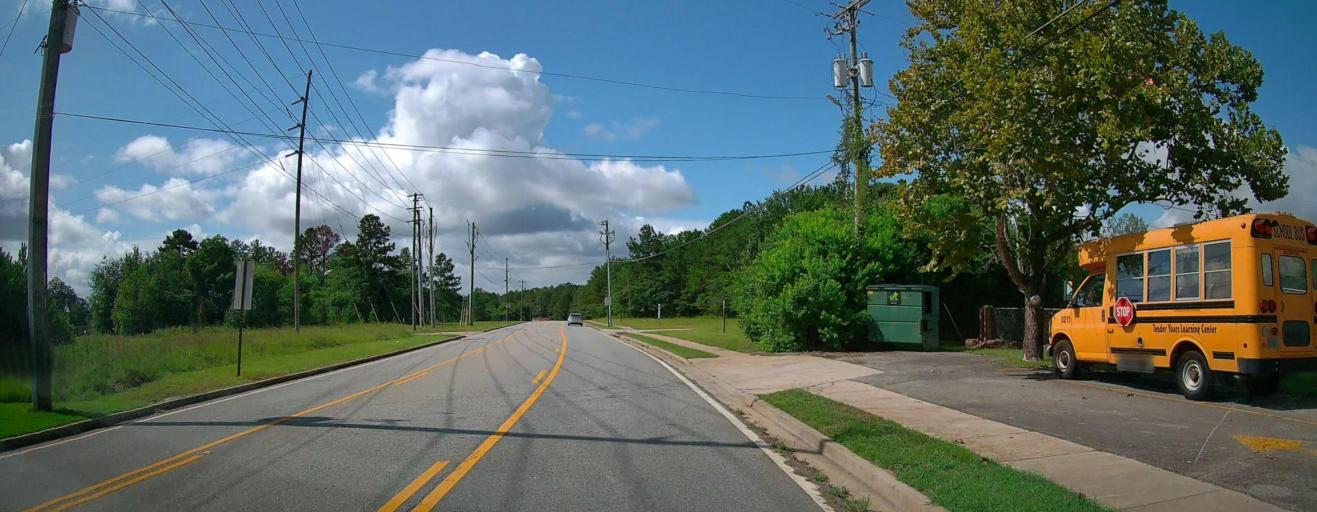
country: US
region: Georgia
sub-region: Houston County
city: Warner Robins
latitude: 32.5929
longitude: -83.6371
